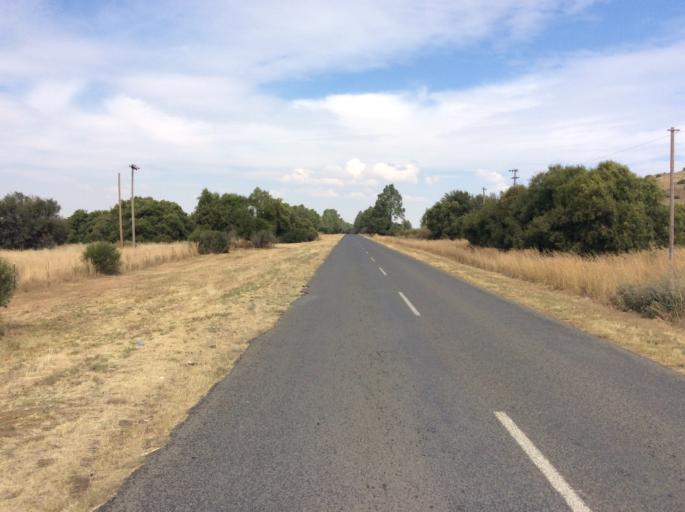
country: ZA
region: Orange Free State
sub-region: Xhariep District Municipality
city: Dewetsdorp
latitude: -29.5648
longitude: 26.6660
